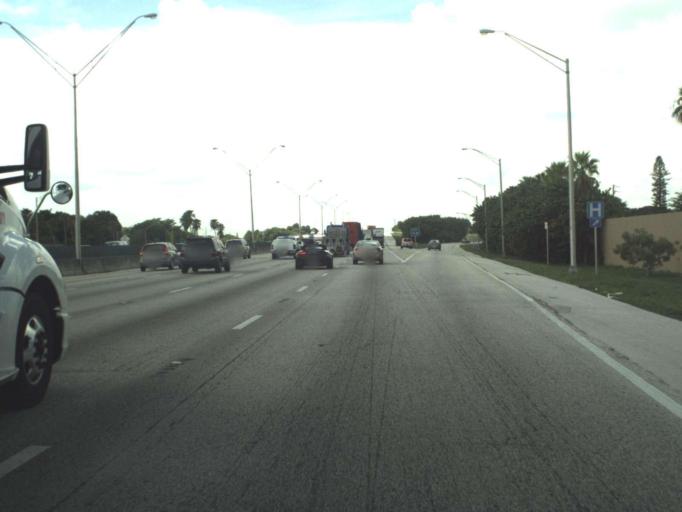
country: US
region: Florida
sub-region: Broward County
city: Tedder
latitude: 26.2806
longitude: -80.1253
